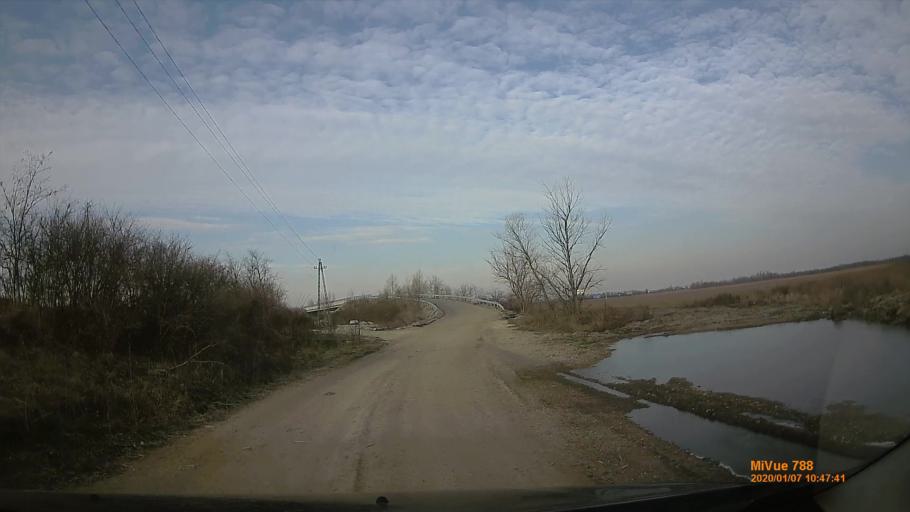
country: HU
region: Gyor-Moson-Sopron
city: Rajka
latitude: 47.9133
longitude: 17.1830
